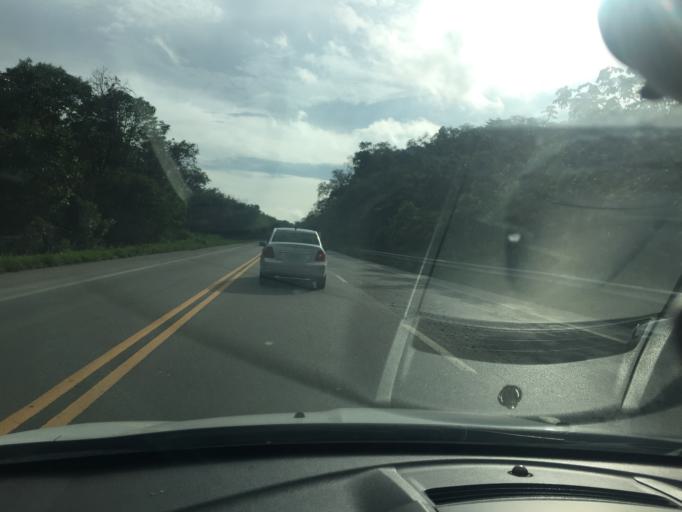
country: BR
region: Sao Paulo
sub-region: Campo Limpo Paulista
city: Campo Limpo Paulista
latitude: -23.1944
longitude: -46.7911
